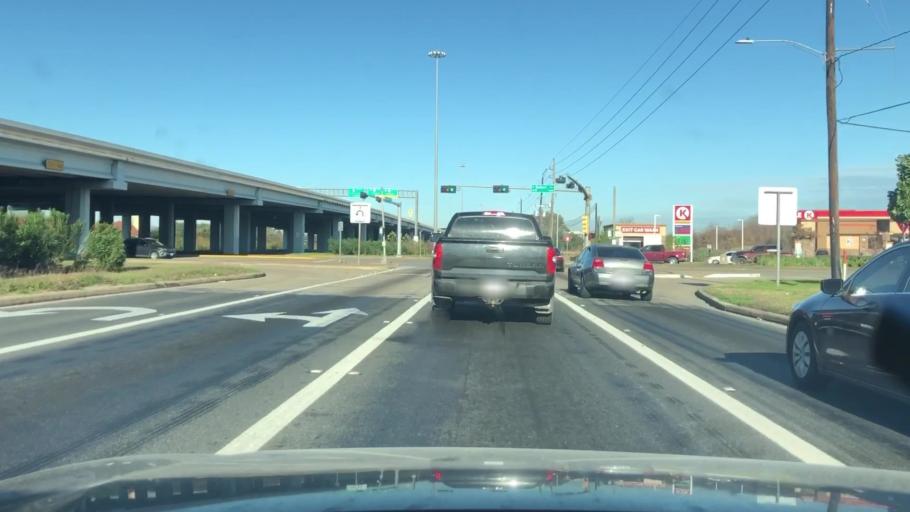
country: US
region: Texas
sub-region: Fort Bend County
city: Missouri City
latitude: 29.6534
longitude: -95.5492
